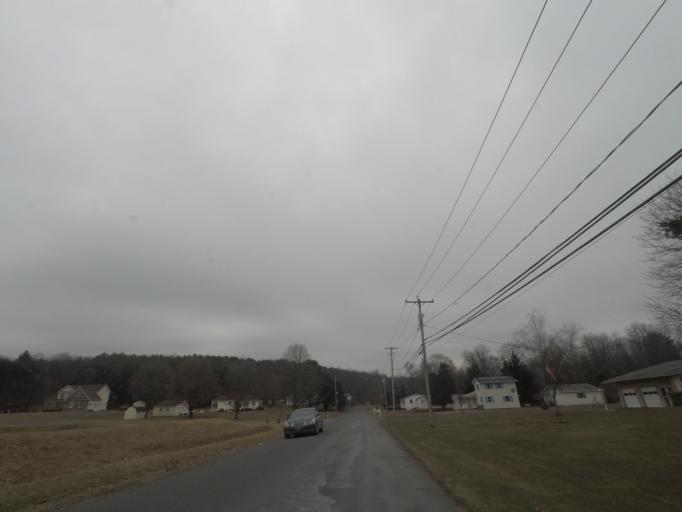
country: US
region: New York
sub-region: Rensselaer County
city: East Greenbush
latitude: 42.5793
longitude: -73.6732
